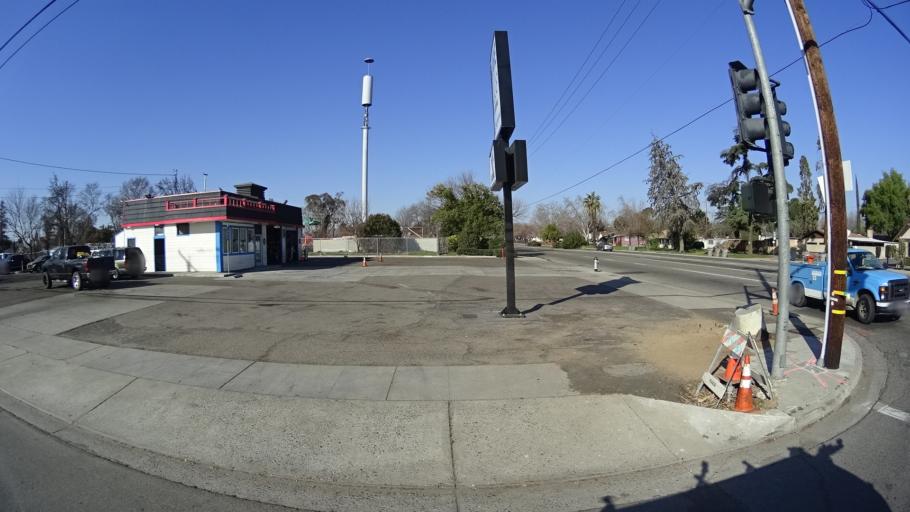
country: US
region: California
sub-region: Fresno County
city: Tarpey Village
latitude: 36.7794
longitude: -119.7365
